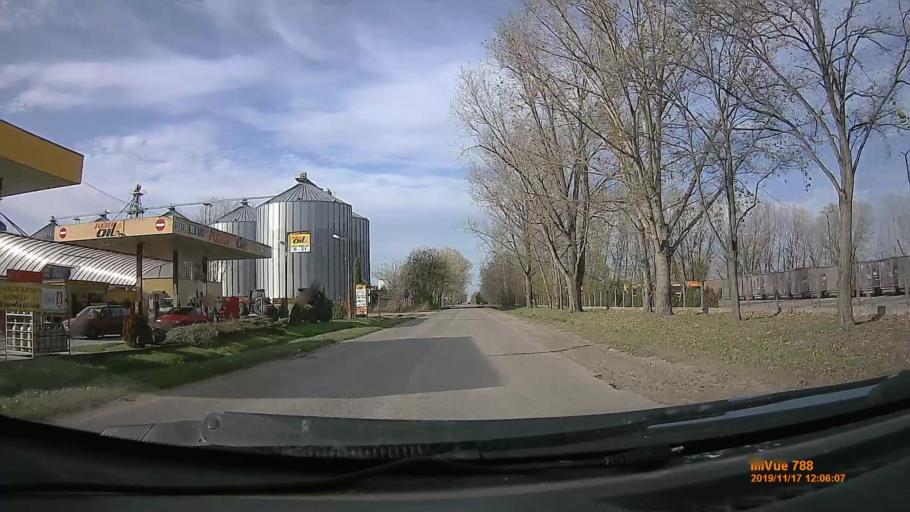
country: HU
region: Bacs-Kiskun
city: Szentkiraly
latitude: 46.9123
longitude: 19.9138
